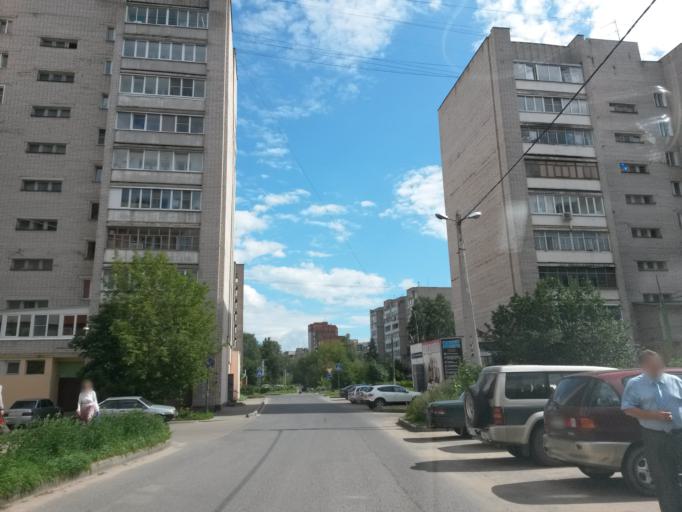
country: RU
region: Ivanovo
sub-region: Gorod Ivanovo
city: Ivanovo
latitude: 56.9918
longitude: 40.9717
